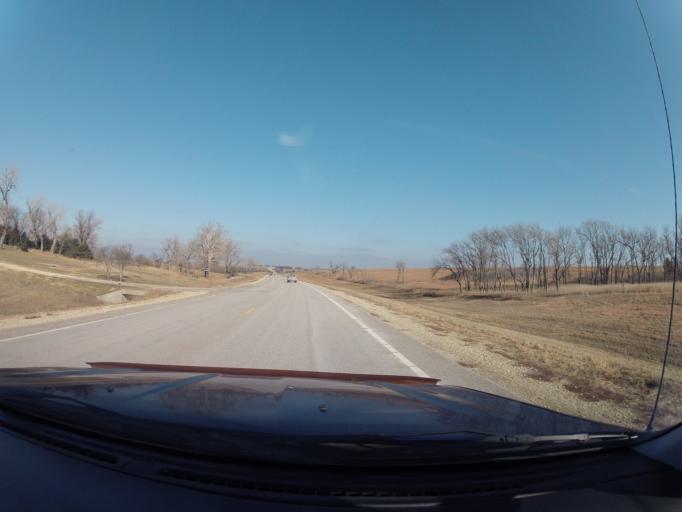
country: US
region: Kansas
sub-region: Marshall County
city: Blue Rapids
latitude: 39.5712
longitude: -96.7506
